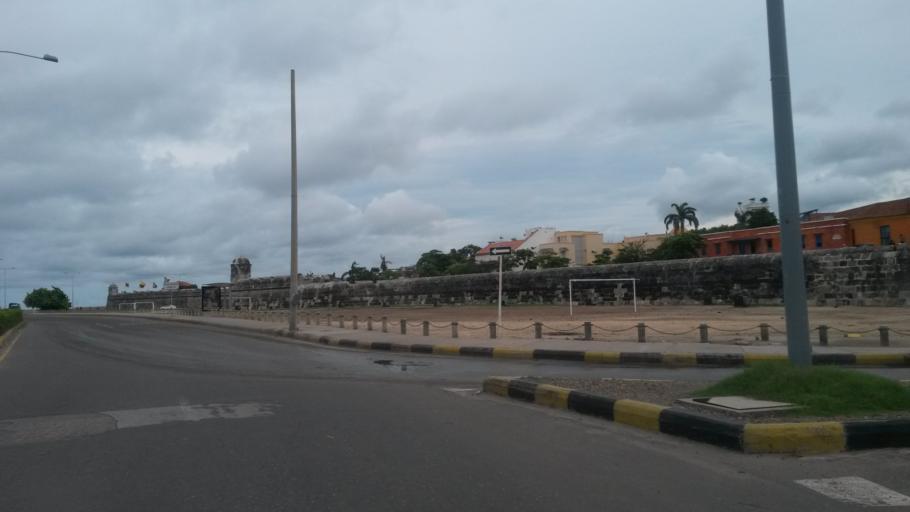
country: CO
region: Bolivar
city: Cartagena
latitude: 10.4217
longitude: -75.5535
